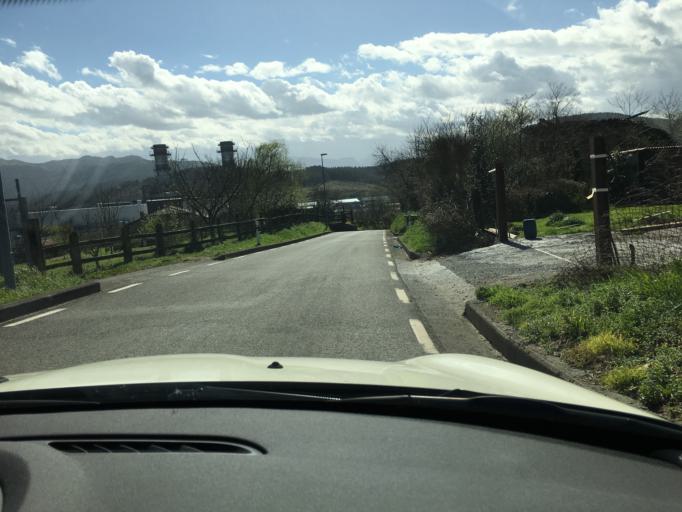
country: ES
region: Basque Country
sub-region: Bizkaia
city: Amorebieta
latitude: 43.2380
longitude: -2.7499
